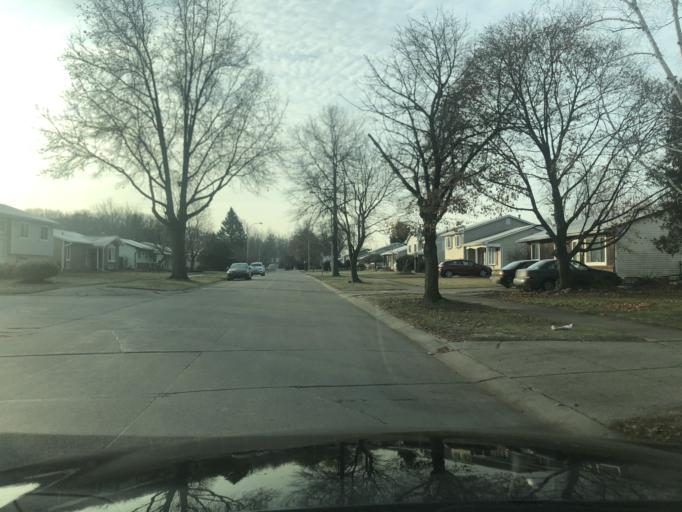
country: US
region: Michigan
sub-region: Wayne County
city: Romulus
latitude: 42.1906
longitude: -83.3351
